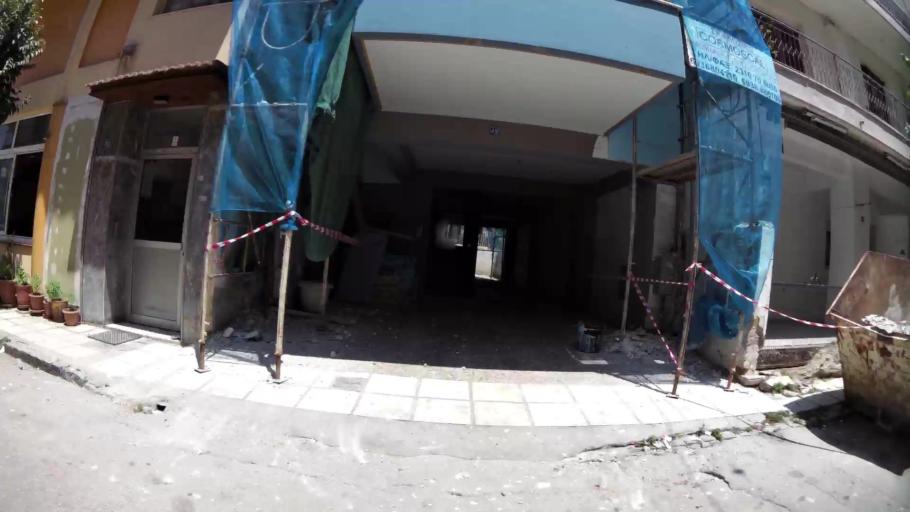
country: GR
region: Central Macedonia
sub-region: Nomos Thessalonikis
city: Evosmos
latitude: 40.6598
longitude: 22.9102
